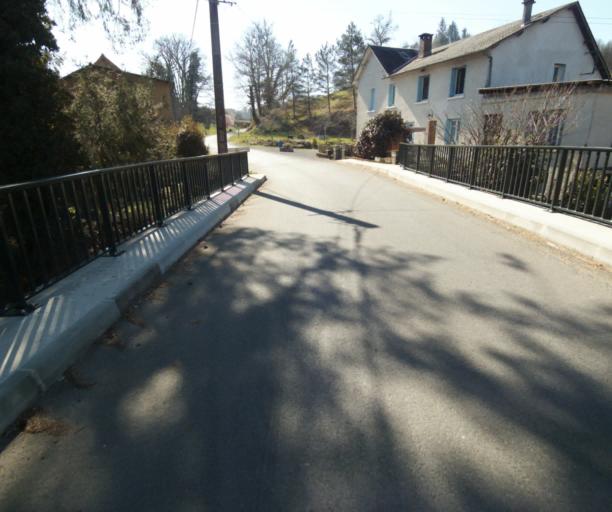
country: FR
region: Limousin
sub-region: Departement de la Correze
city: Saint-Mexant
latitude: 45.2931
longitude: 1.6165
